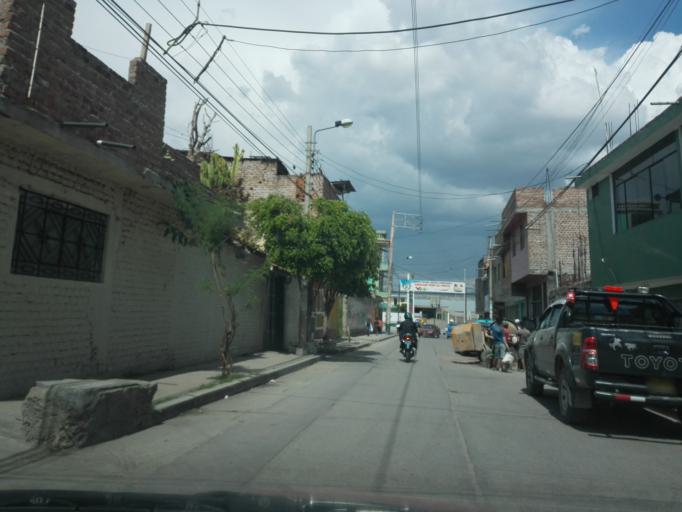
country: PE
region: Ayacucho
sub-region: Provincia de Huamanga
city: Ayacucho
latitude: -13.1631
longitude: -74.2165
